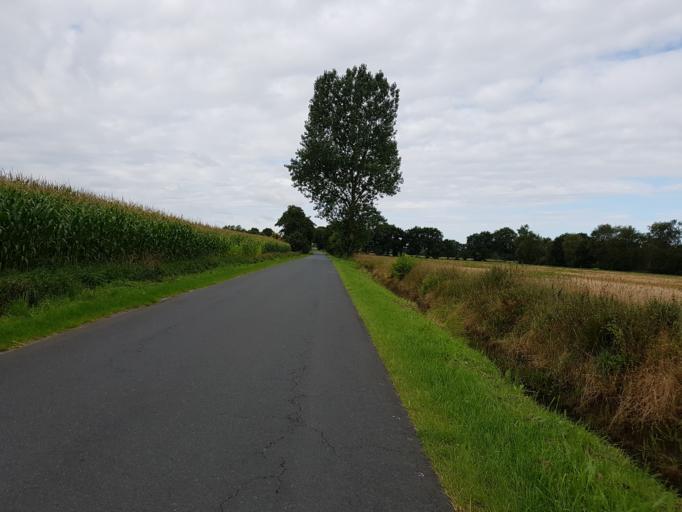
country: DE
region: Lower Saxony
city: Wittmund
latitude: 53.5577
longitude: 7.7194
